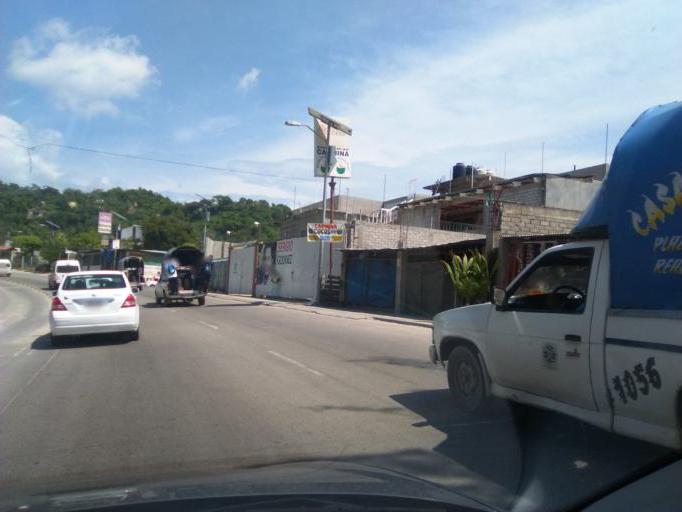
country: MX
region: Guerrero
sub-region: Acapulco de Juarez
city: Colonia Nueva Revolucion
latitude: 16.9113
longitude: -99.8209
